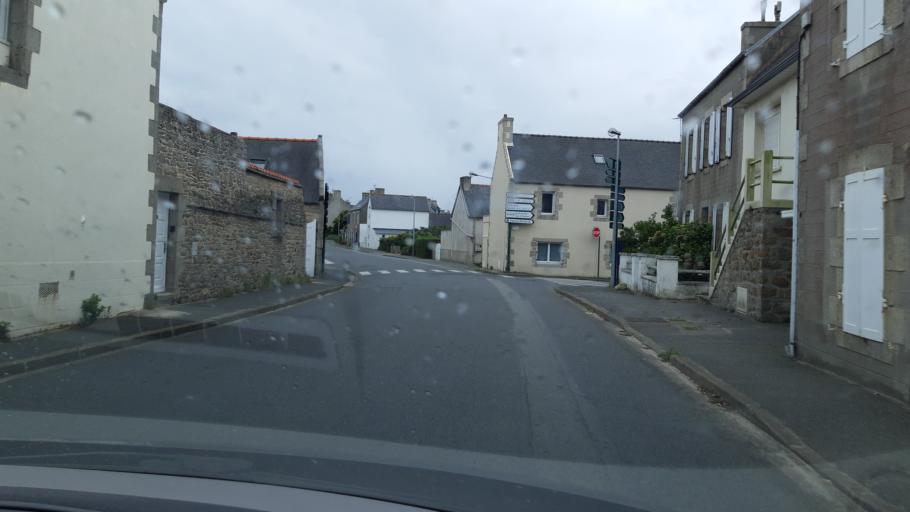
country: FR
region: Brittany
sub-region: Departement du Finistere
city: Roscoff
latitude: 48.7179
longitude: -3.9851
